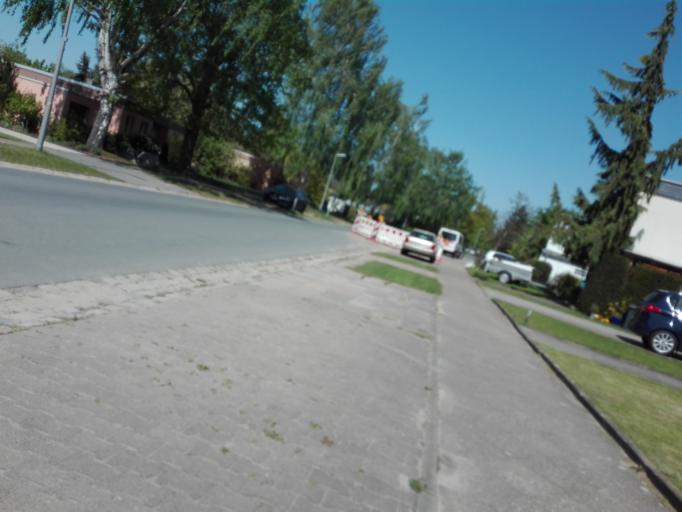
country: DE
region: Berlin
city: Rudow
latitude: 52.4042
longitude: 13.4827
